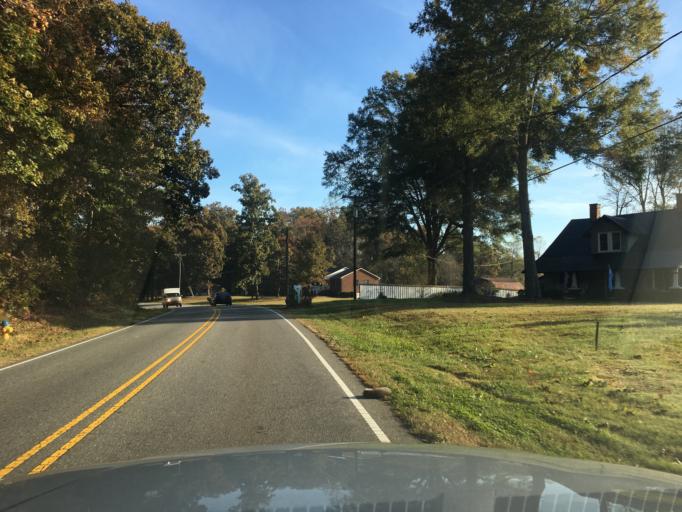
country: US
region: North Carolina
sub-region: Catawba County
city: Newton
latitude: 35.6716
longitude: -81.2457
